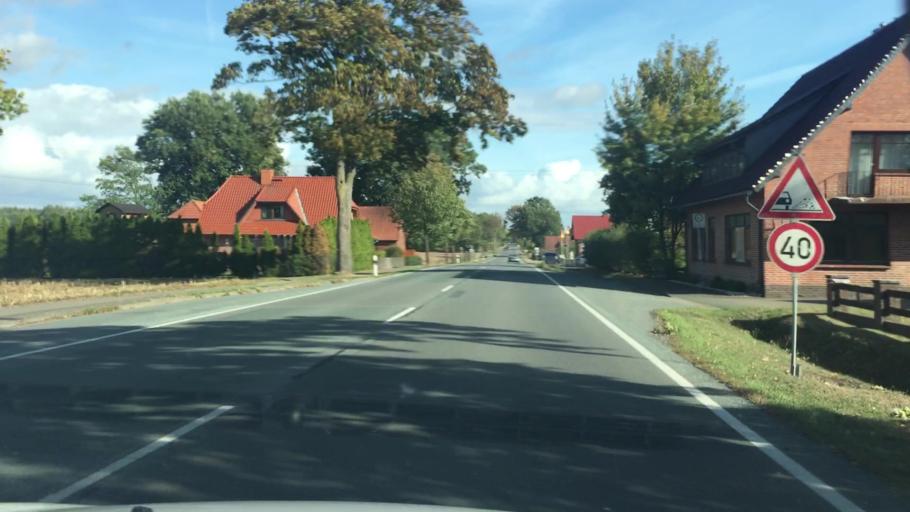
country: DE
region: Lower Saxony
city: Pennigsehl
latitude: 52.6654
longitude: 9.0114
